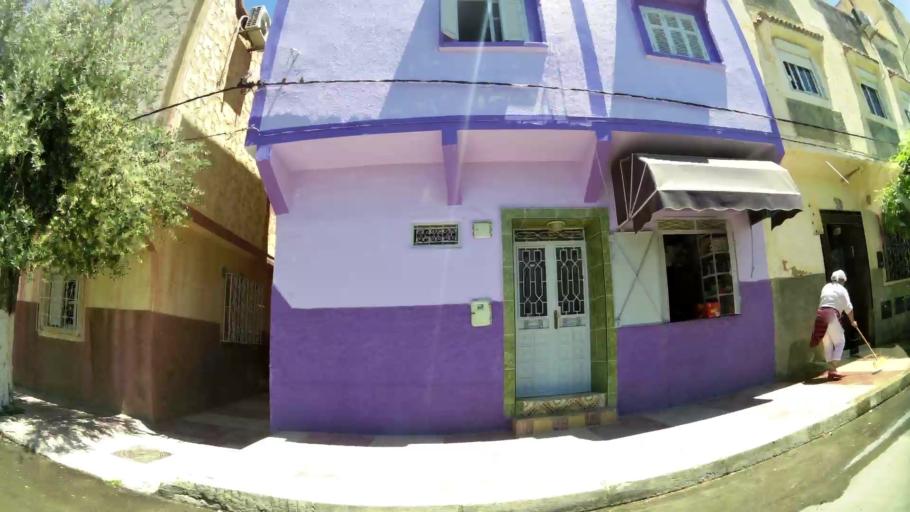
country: MA
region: Meknes-Tafilalet
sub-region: Meknes
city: Meknes
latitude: 33.9056
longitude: -5.5647
